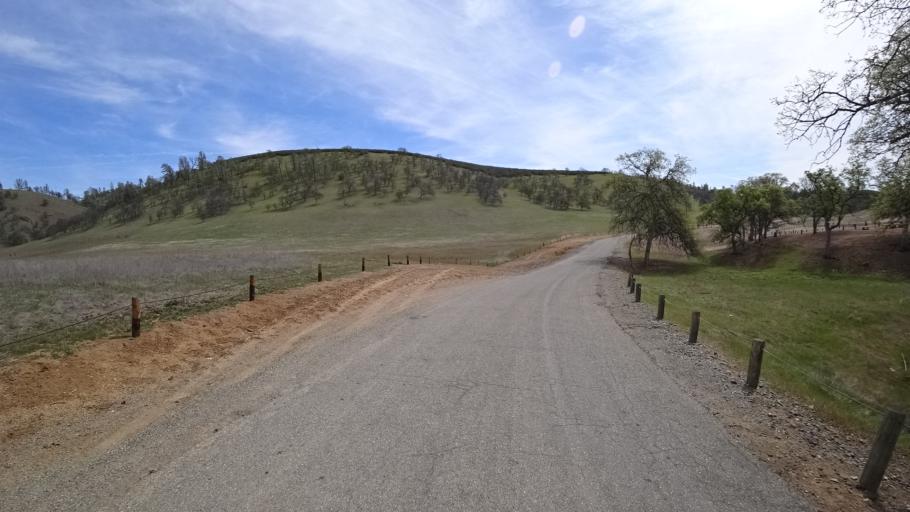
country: US
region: California
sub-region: Glenn County
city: Willows
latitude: 39.5940
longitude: -122.5255
